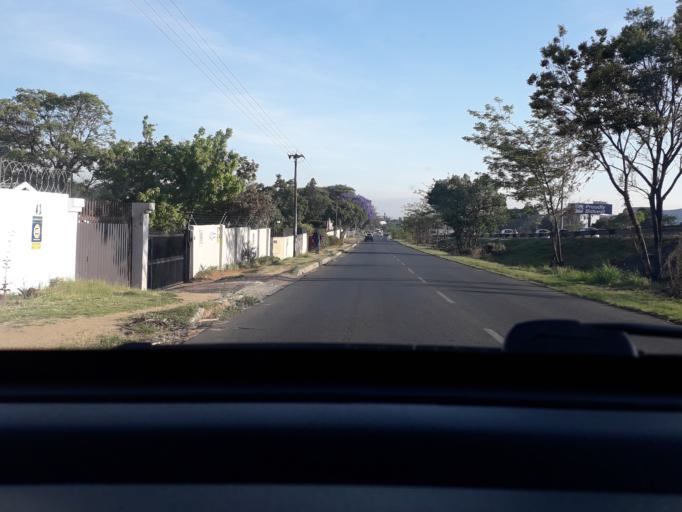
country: ZA
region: Gauteng
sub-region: City of Johannesburg Metropolitan Municipality
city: Modderfontein
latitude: -26.0809
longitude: 28.0867
